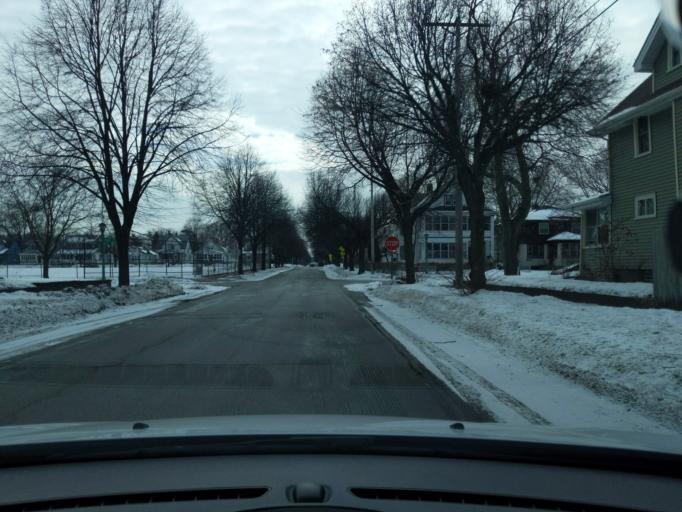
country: US
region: Minnesota
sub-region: Ramsey County
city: Falcon Heights
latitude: 44.9615
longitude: -93.1620
